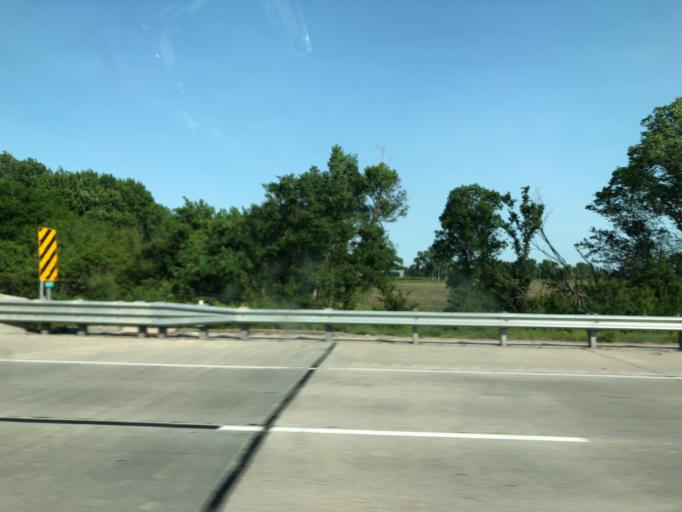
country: US
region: Nebraska
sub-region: Saunders County
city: Ashland
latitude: 40.9832
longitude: -96.3722
